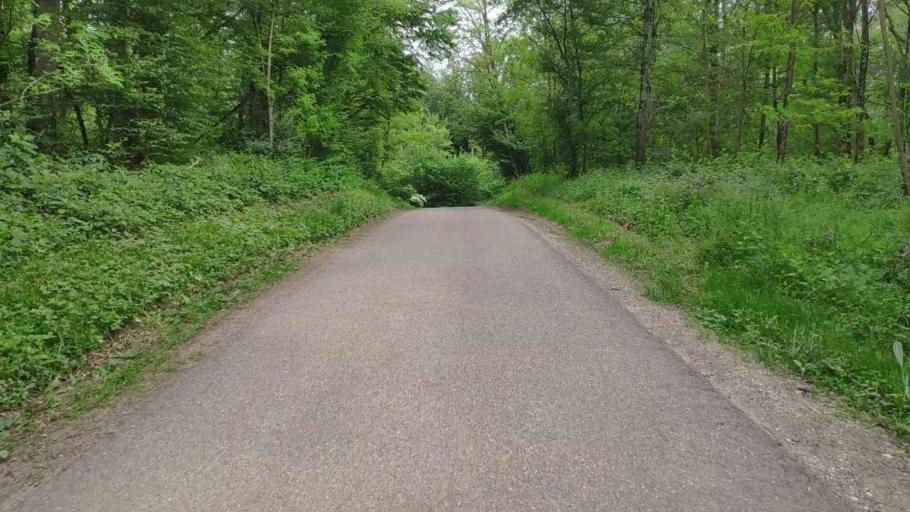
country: FR
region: Franche-Comte
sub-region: Departement du Jura
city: Montmorot
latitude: 46.7471
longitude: 5.5324
